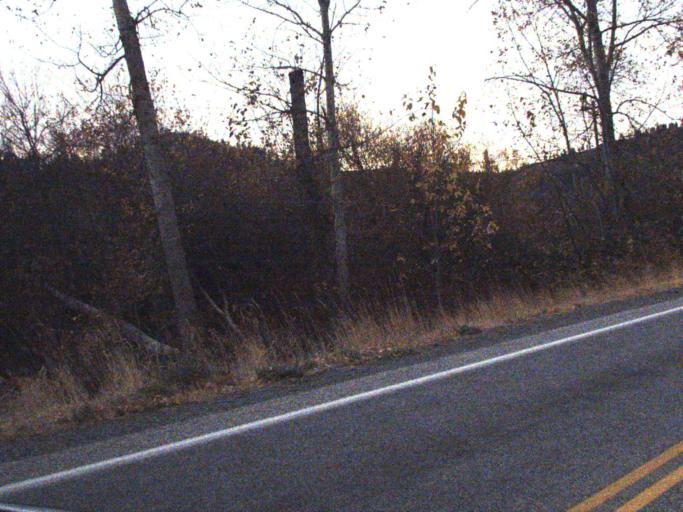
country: US
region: Washington
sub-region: Ferry County
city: Republic
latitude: 48.6514
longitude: -118.6918
